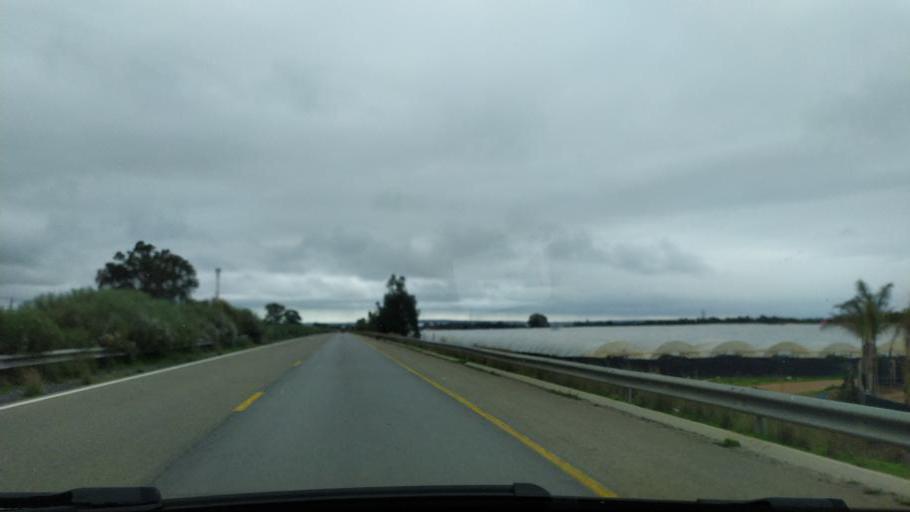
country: MA
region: Gharb-Chrarda-Beni Hssen
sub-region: Kenitra Province
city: Lalla Mimouna
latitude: 34.8933
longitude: -6.2100
